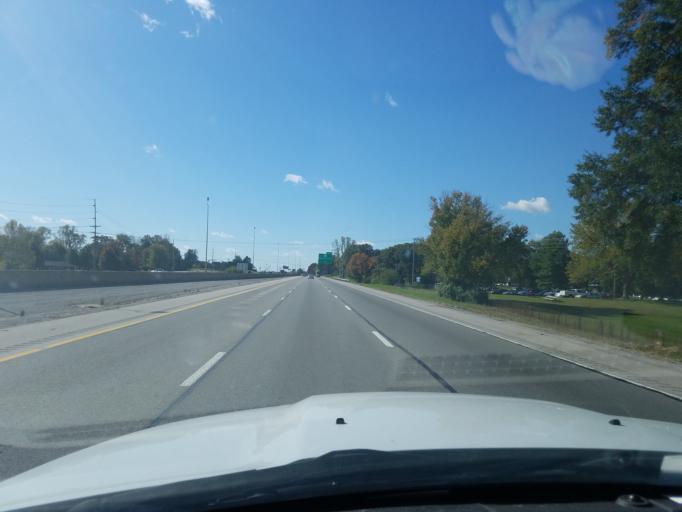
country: US
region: Kentucky
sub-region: Warren County
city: Bowling Green
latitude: 36.9527
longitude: -86.4069
